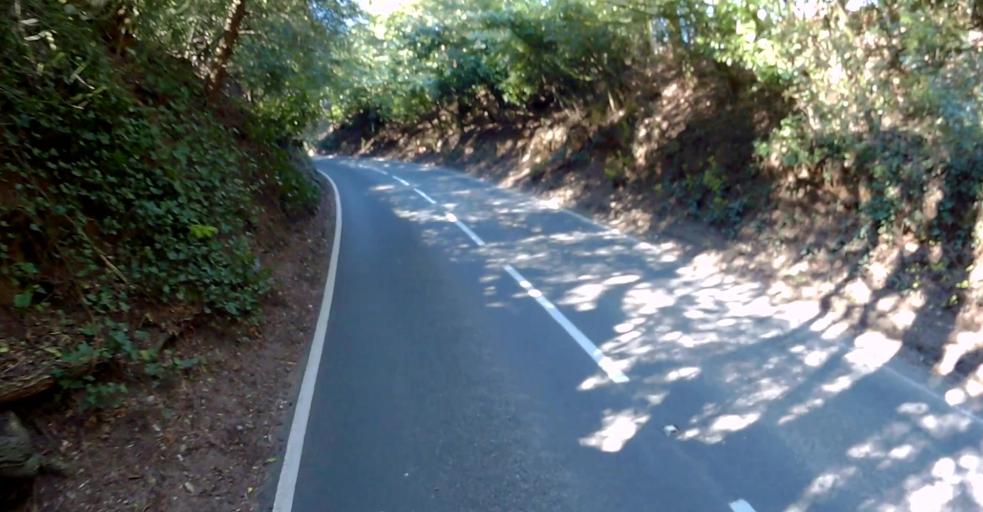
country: GB
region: England
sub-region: Surrey
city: Farnham
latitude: 51.2044
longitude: -0.7784
